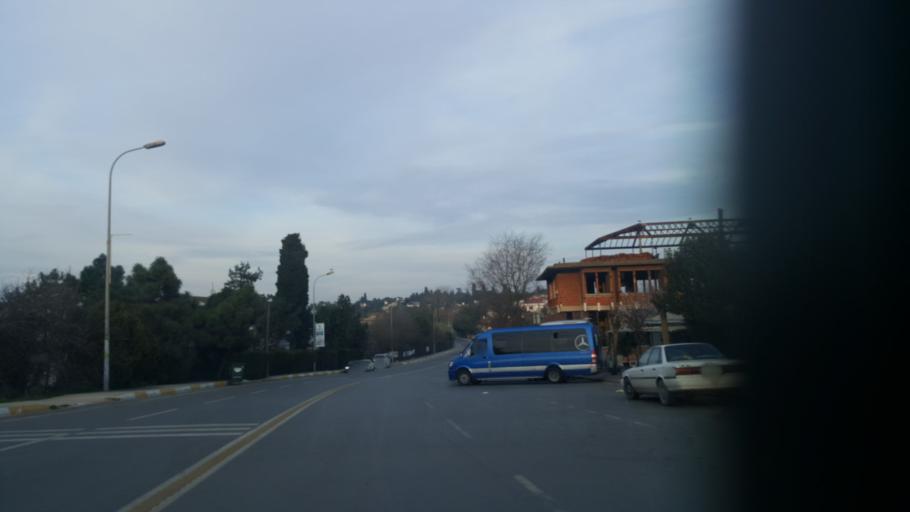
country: TR
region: Istanbul
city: Icmeler
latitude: 40.8170
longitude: 29.2726
